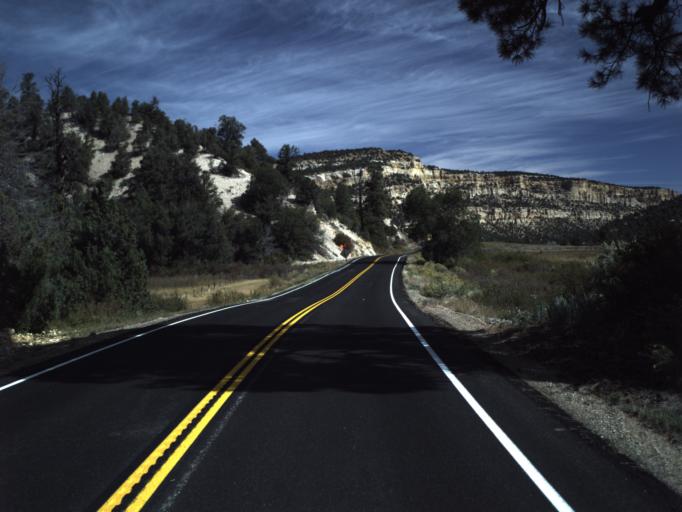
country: US
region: Utah
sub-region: Garfield County
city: Panguitch
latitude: 37.7154
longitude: -111.7850
